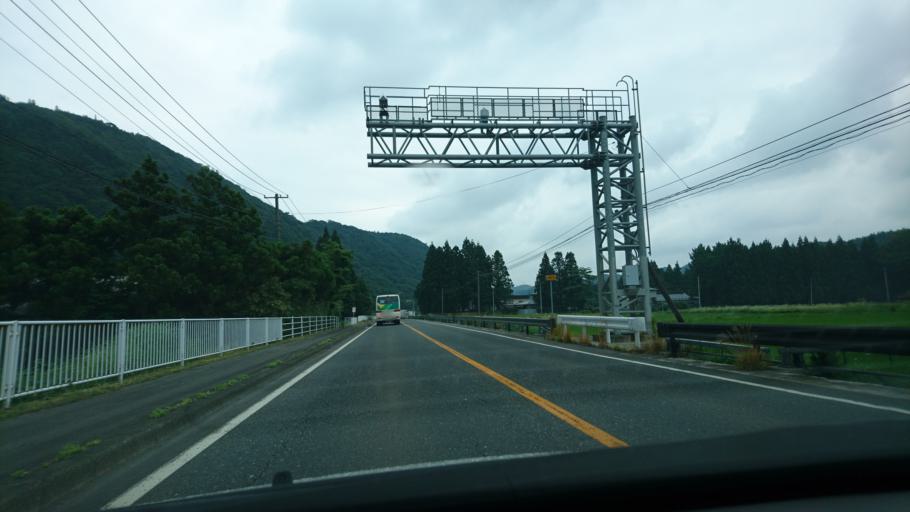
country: JP
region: Miyagi
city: Furukawa
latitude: 38.7258
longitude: 140.7982
